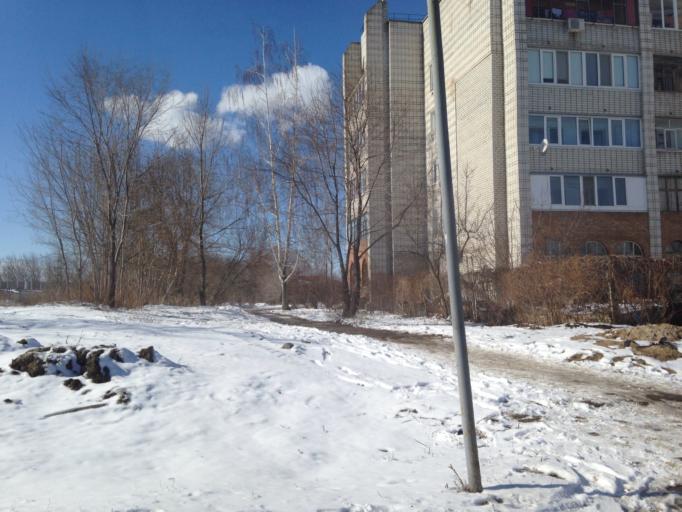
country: RU
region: Ulyanovsk
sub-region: Ulyanovskiy Rayon
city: Ulyanovsk
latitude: 54.3253
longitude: 48.4712
